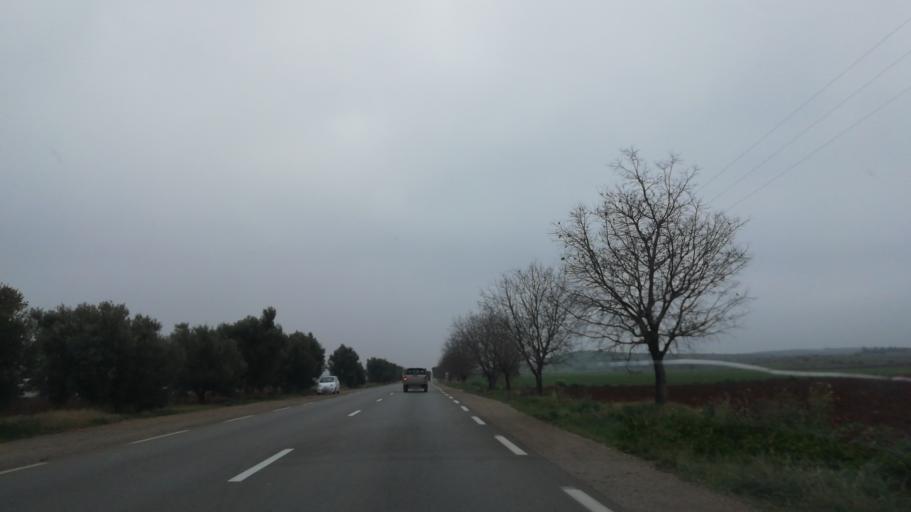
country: DZ
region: Mascara
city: Mascara
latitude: 35.3126
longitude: 0.3899
